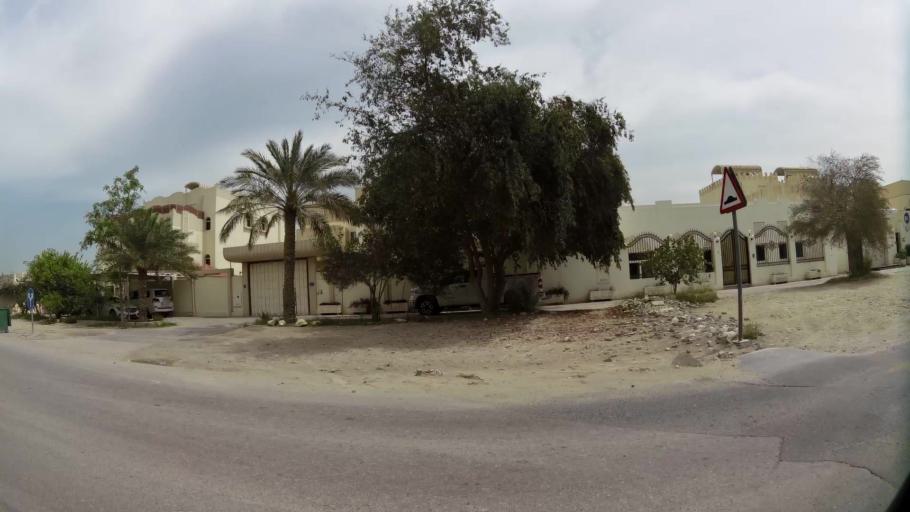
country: QA
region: Baladiyat ar Rayyan
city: Ar Rayyan
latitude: 25.2788
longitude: 51.4605
